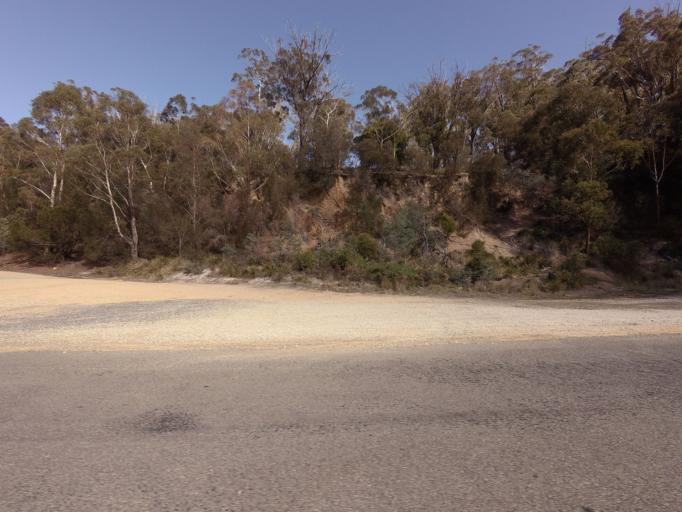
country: AU
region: Tasmania
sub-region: Break O'Day
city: St Helens
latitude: -41.6663
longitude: 148.2629
